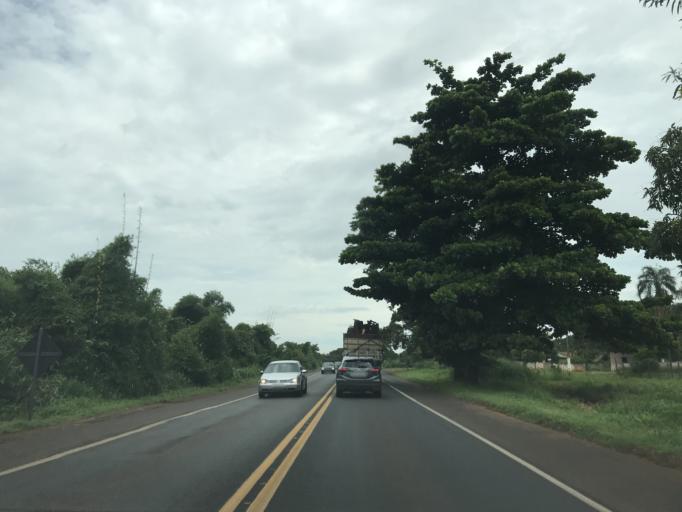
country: BR
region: Sao Paulo
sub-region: Nova Granada
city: Nova Granada
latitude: -20.2537
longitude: -49.1722
